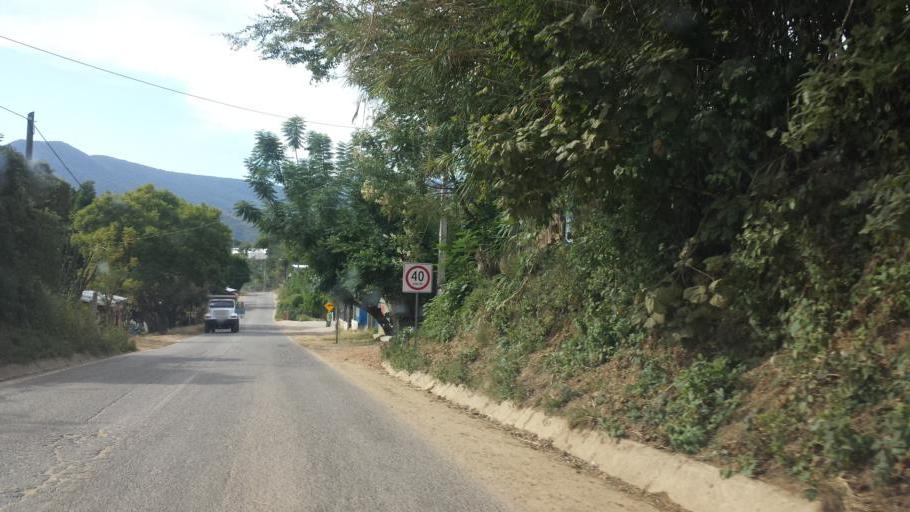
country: MX
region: Oaxaca
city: La Pe
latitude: 16.6154
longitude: -96.8559
